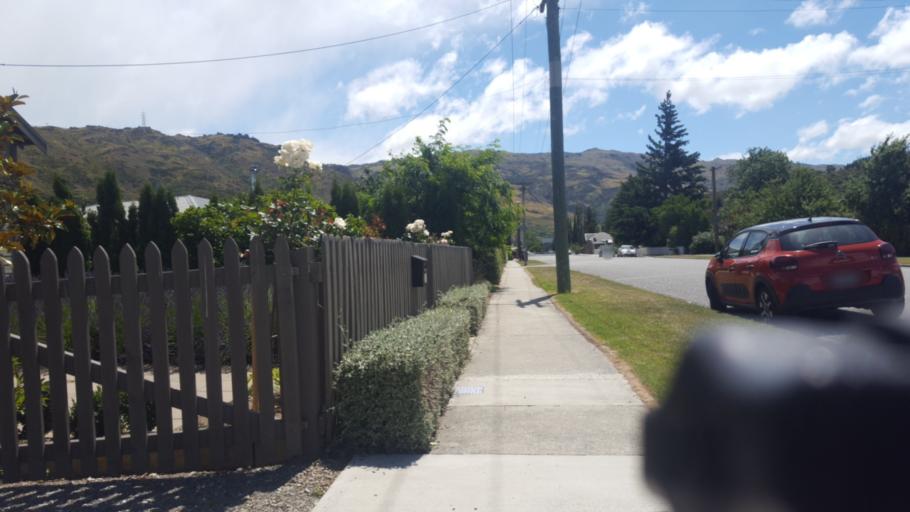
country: NZ
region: Otago
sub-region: Queenstown-Lakes District
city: Wanaka
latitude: -45.1905
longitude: 169.3188
